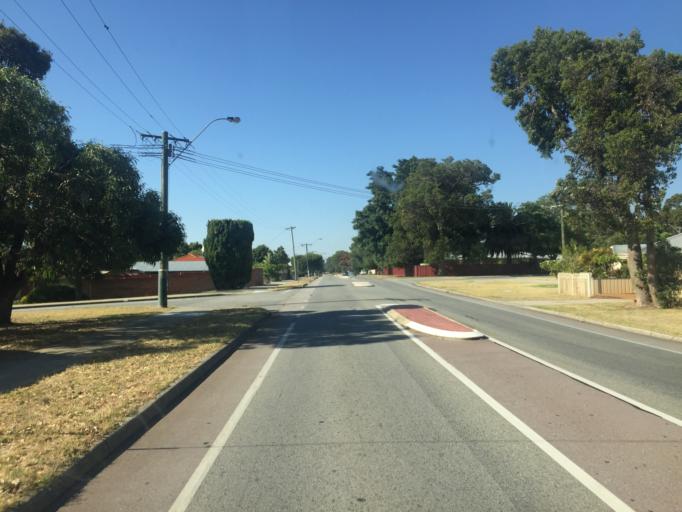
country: AU
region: Western Australia
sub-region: Gosnells
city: Maddington
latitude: -32.0370
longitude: 115.9821
